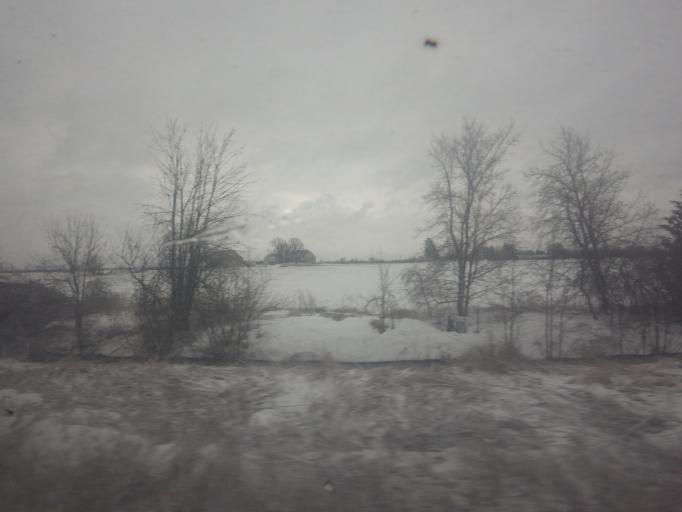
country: CA
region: Ontario
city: Bells Corners
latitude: 45.2015
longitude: -75.8143
